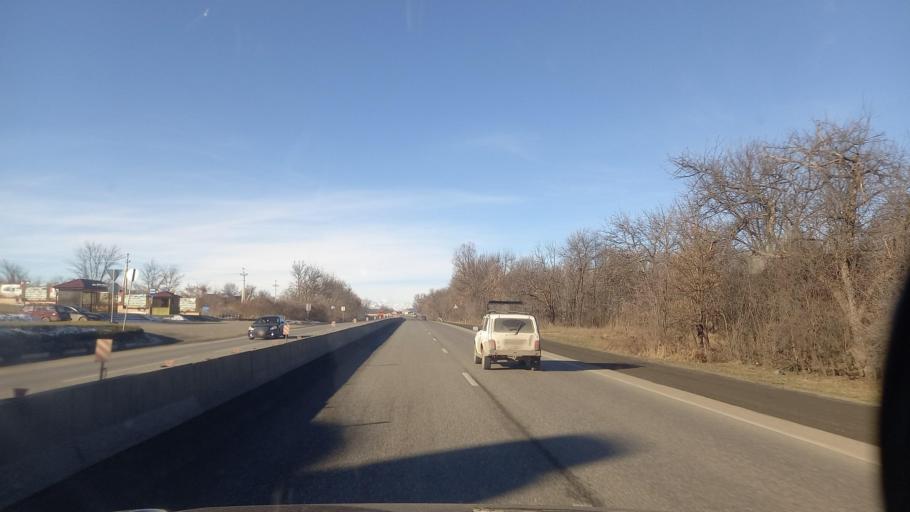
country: RU
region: North Ossetia
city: Gizel'
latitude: 43.0288
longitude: 44.5855
